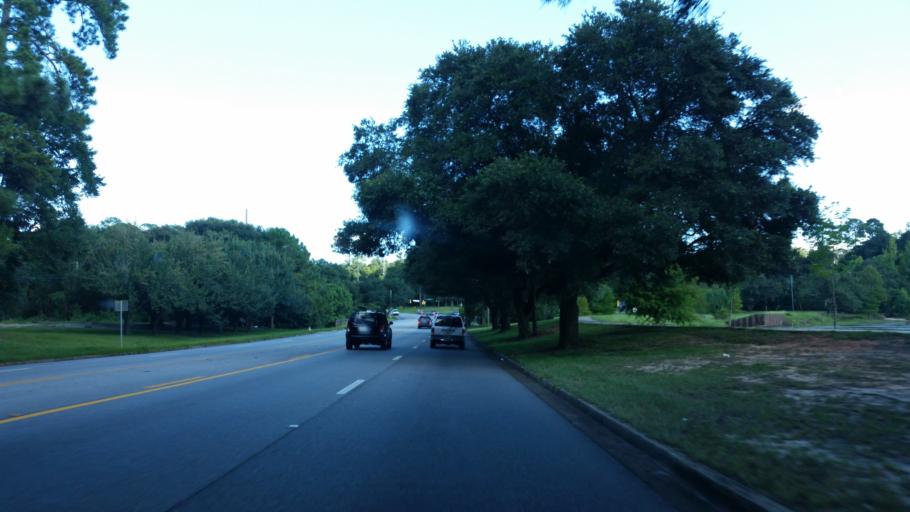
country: US
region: Alabama
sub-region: Mobile County
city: Prichard
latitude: 30.7073
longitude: -88.1523
